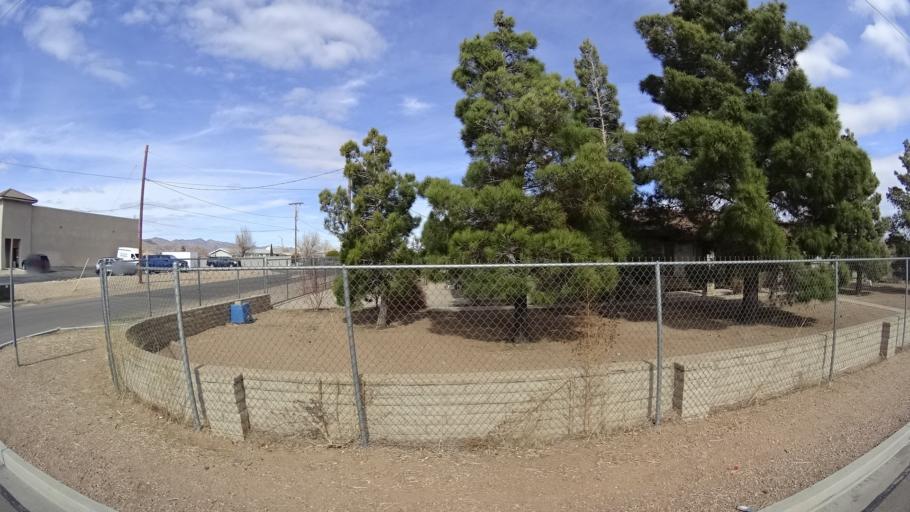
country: US
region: Arizona
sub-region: Mohave County
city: New Kingman-Butler
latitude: 35.2394
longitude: -114.0264
